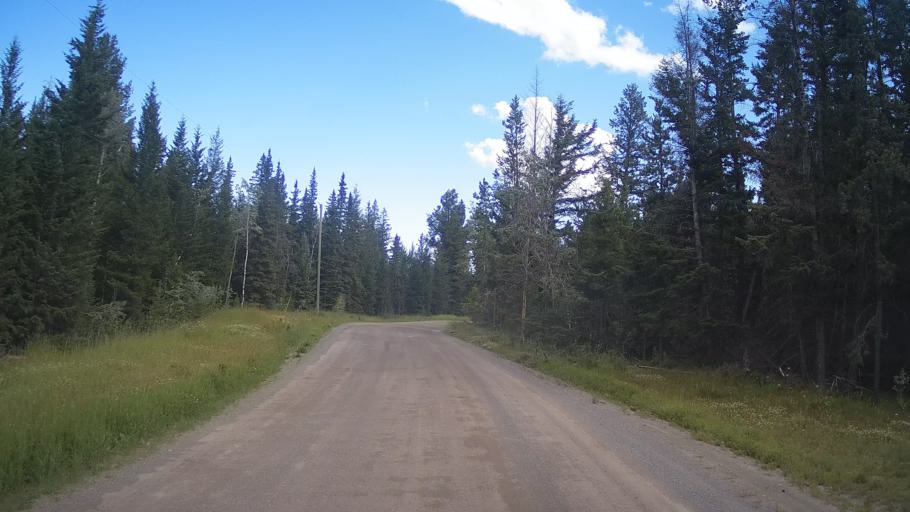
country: CA
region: British Columbia
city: Cache Creek
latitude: 51.1949
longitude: -121.5899
